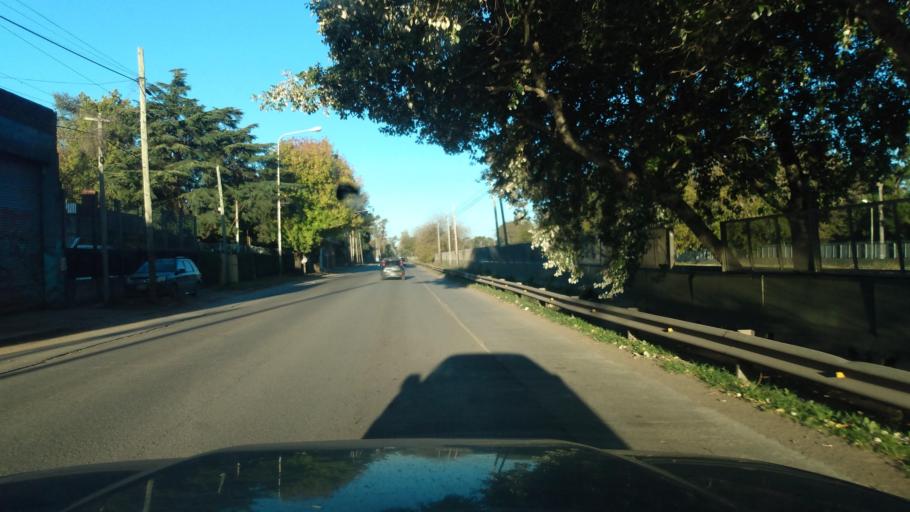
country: AR
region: Buenos Aires
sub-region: Partido de Merlo
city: Merlo
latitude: -34.6405
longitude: -58.8249
